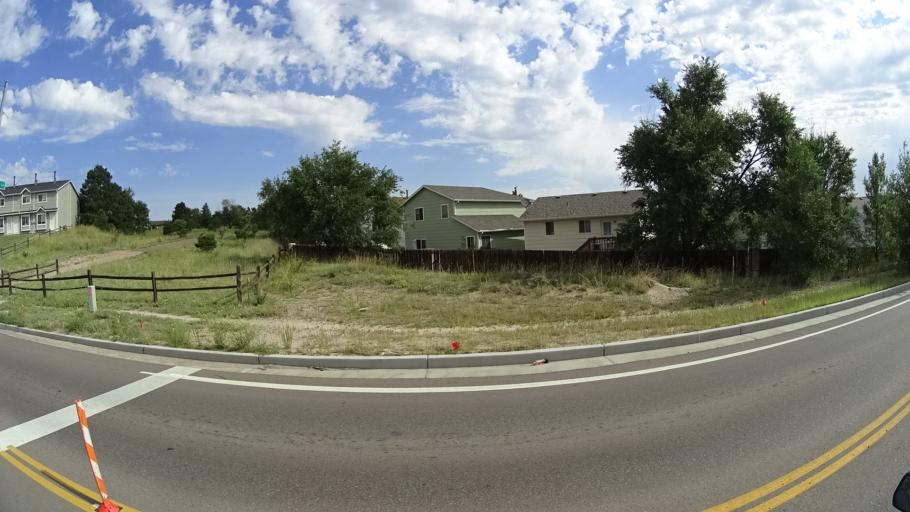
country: US
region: Colorado
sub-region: El Paso County
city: Cimarron Hills
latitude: 38.8954
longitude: -104.7268
